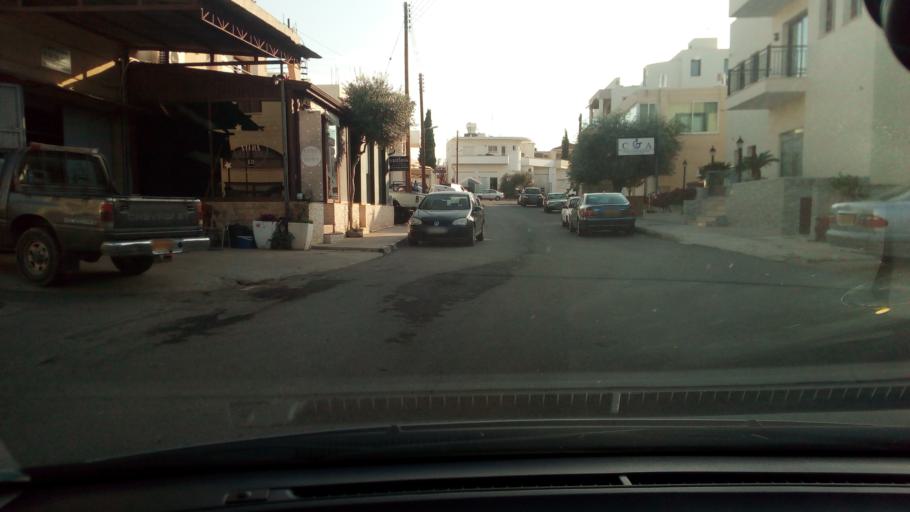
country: CY
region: Pafos
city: Polis
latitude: 35.0369
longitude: 32.4279
